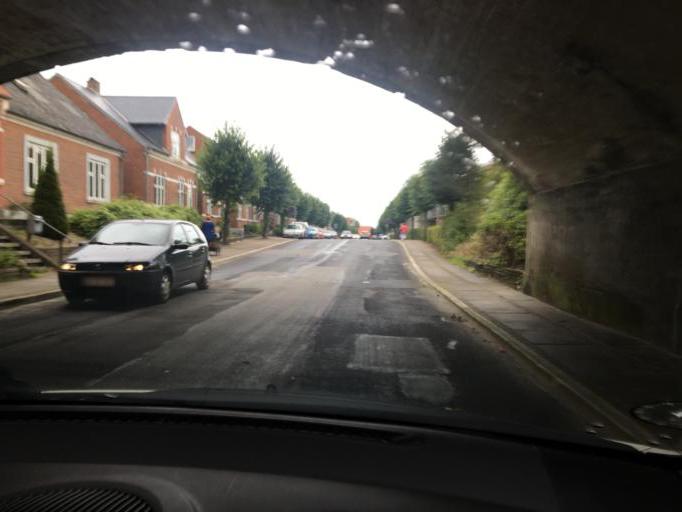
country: DK
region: South Denmark
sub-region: Middelfart Kommune
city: Middelfart
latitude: 55.5018
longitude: 9.7268
